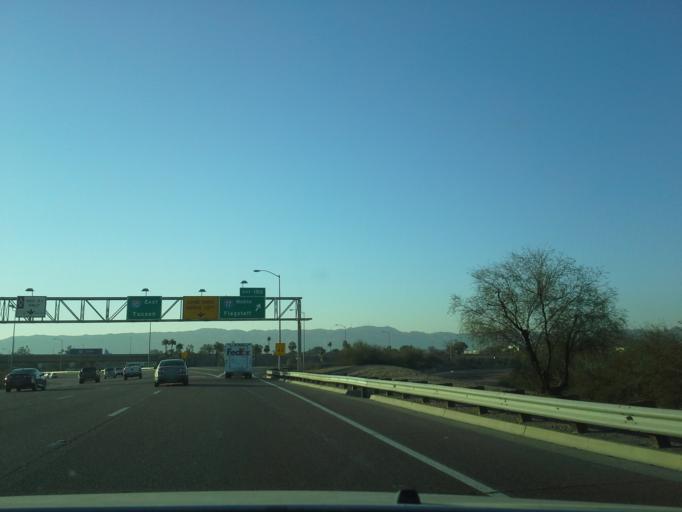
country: US
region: Arizona
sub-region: Maricopa County
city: Phoenix
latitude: 33.4310
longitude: -112.0379
